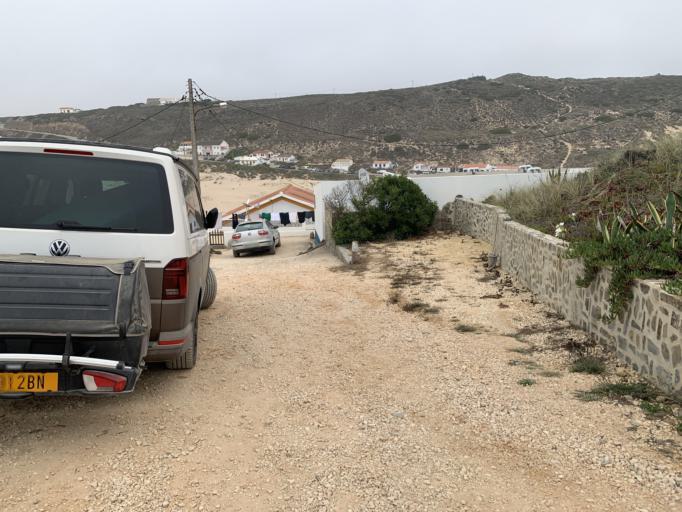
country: PT
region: Faro
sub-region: Aljezur
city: Aljezur
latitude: 37.3401
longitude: -8.8546
